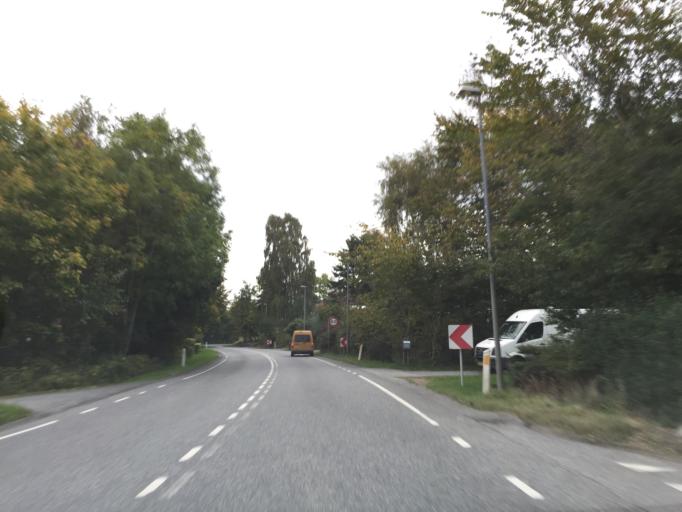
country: DK
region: Central Jutland
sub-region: Viborg Kommune
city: Bjerringbro
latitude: 56.3139
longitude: 9.6887
